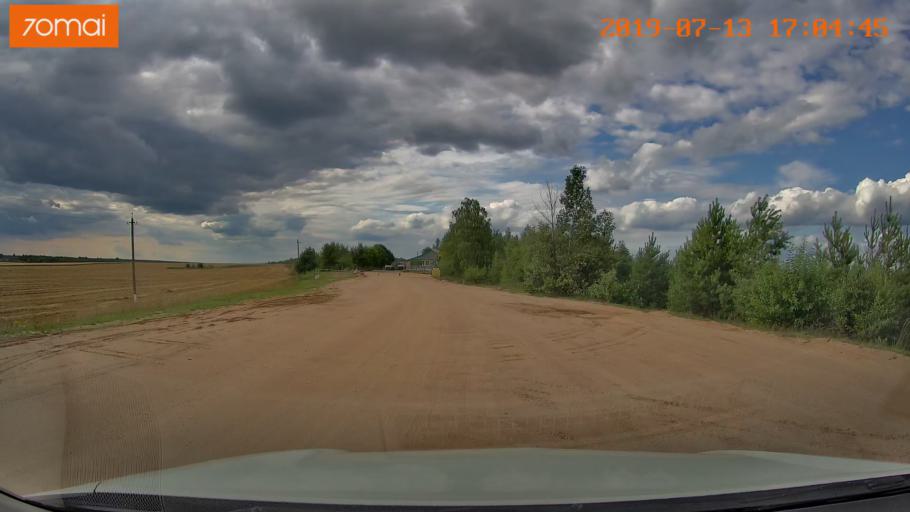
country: BY
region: Mogilev
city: Kirawsk
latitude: 53.2719
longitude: 29.3678
